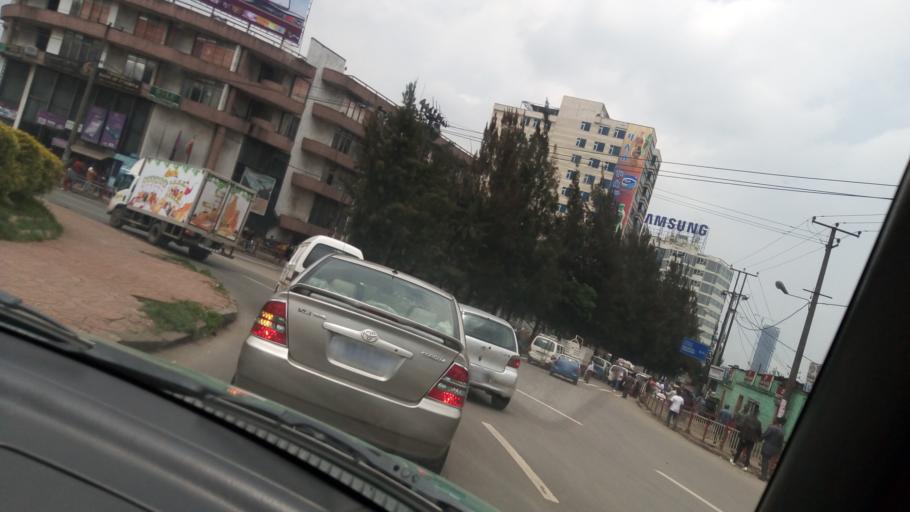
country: ET
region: Adis Abeba
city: Addis Ababa
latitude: 9.0284
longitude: 38.7433
